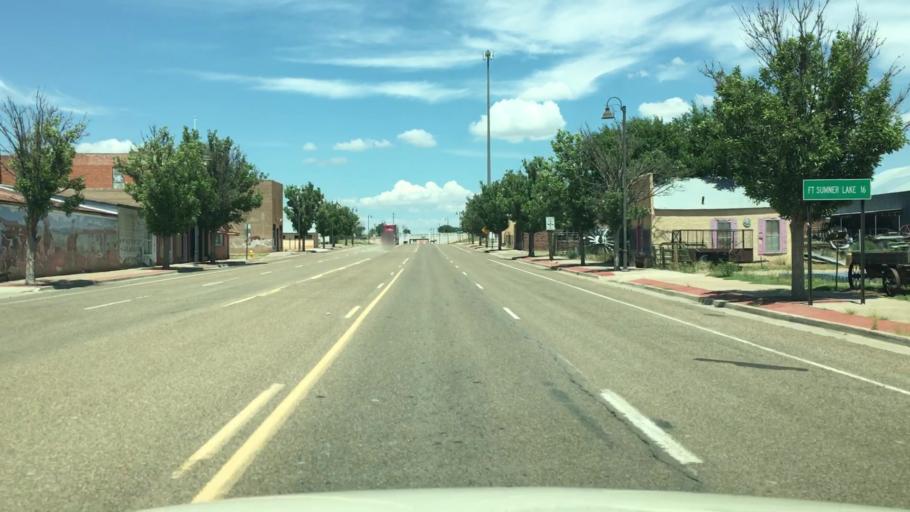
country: US
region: New Mexico
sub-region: De Baca County
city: Fort Sumner
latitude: 34.4730
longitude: -104.2453
